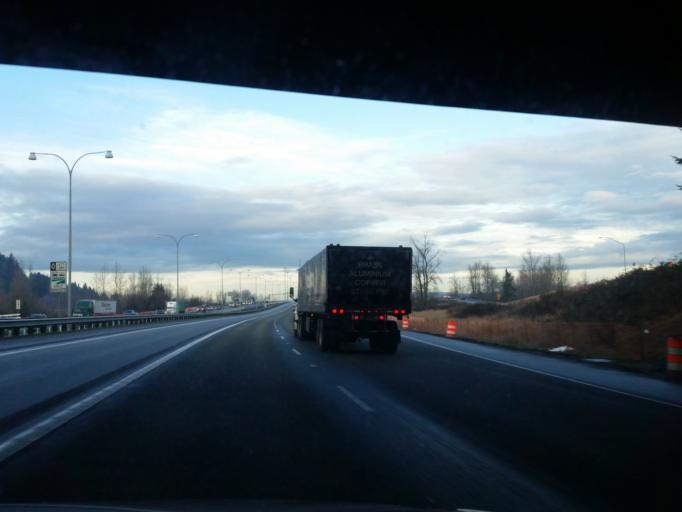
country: US
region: Washington
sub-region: King County
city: Algona
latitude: 47.2958
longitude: -122.2567
